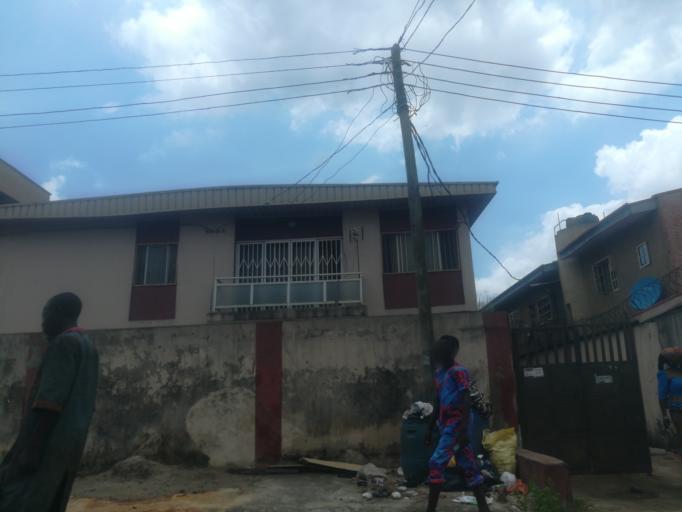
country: NG
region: Lagos
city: Ojota
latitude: 6.5653
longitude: 3.3895
